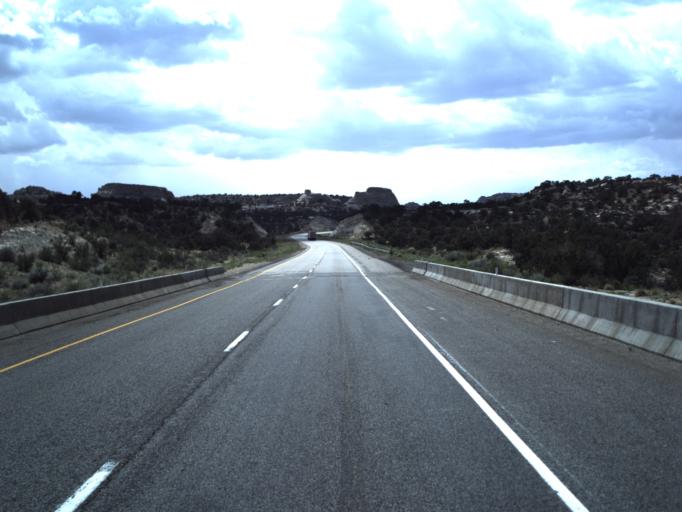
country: US
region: Utah
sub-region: Emery County
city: Ferron
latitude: 38.8606
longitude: -110.8664
